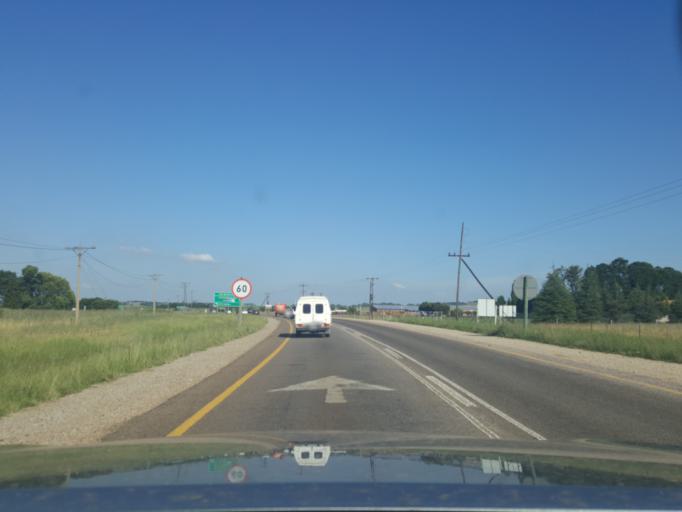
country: ZA
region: Gauteng
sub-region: City of Tshwane Metropolitan Municipality
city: Cullinan
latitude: -25.7908
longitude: 28.5144
